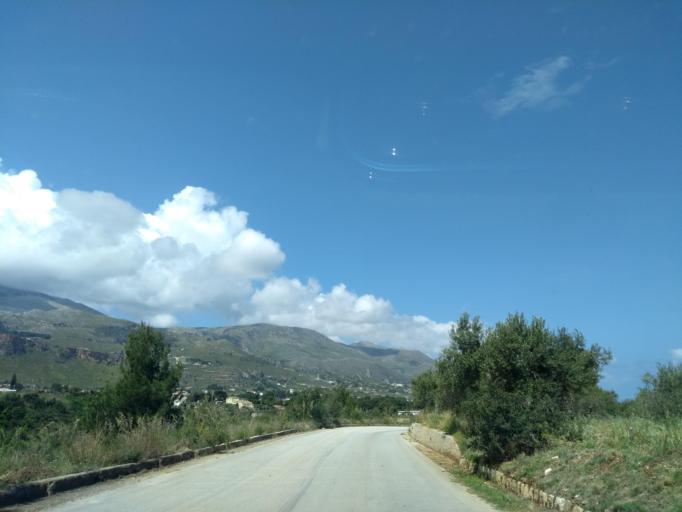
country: IT
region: Sicily
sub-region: Trapani
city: Castellammare del Golfo
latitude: 38.0486
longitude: 12.8419
